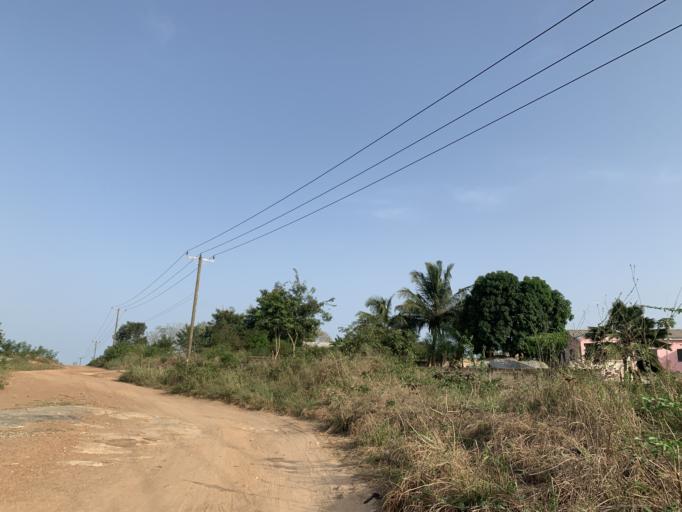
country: GH
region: Central
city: Winneba
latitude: 5.3791
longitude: -0.6165
